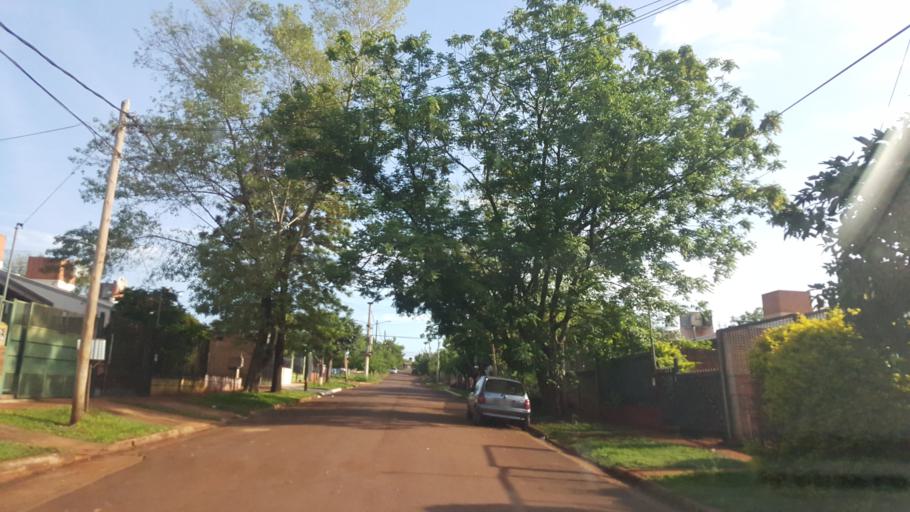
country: AR
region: Misiones
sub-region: Departamento de Capital
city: Posadas
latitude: -27.4235
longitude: -55.9236
